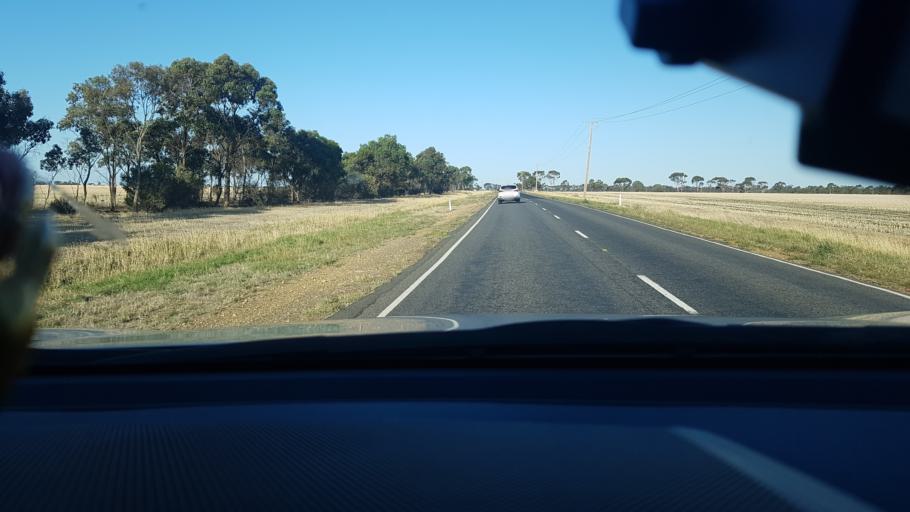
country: AU
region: Victoria
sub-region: Horsham
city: Horsham
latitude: -36.7321
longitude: 142.1378
